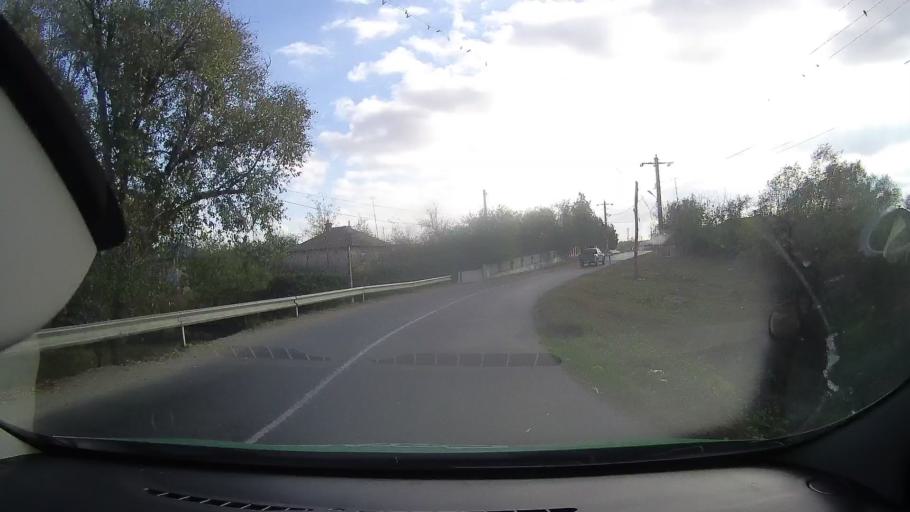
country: RO
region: Constanta
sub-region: Comuna Sacele
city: Sacele
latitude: 44.4858
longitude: 28.6451
